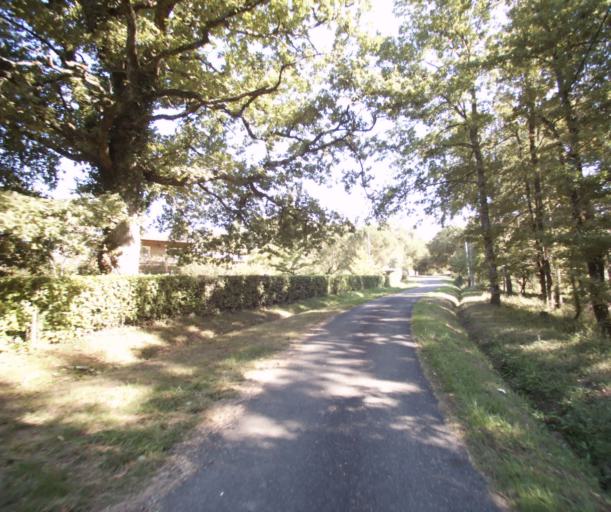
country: FR
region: Midi-Pyrenees
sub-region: Departement du Gers
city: Cazaubon
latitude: 43.9445
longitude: -0.0468
